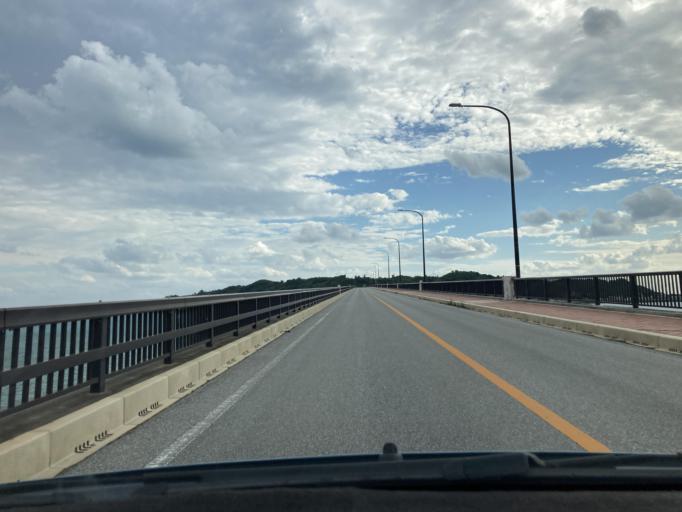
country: JP
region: Okinawa
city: Katsuren-haebaru
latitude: 26.3364
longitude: 127.9553
